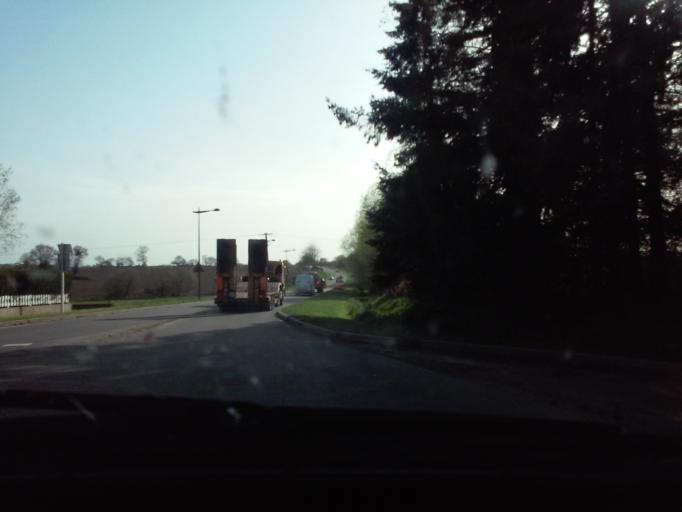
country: FR
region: Brittany
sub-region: Departement d'Ille-et-Vilaine
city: Saint-Jean-sur-Couesnon
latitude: 48.2878
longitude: -1.3720
